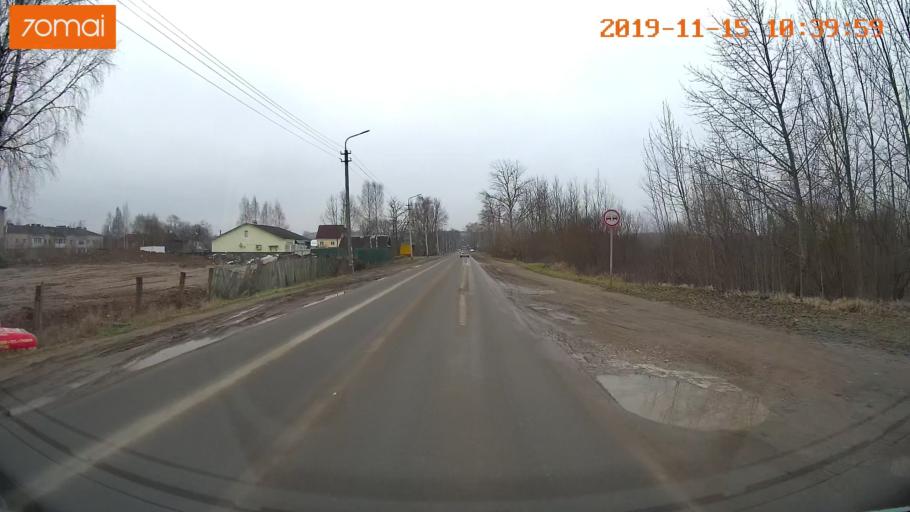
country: RU
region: Vologda
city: Sheksna
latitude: 59.2176
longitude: 38.5106
